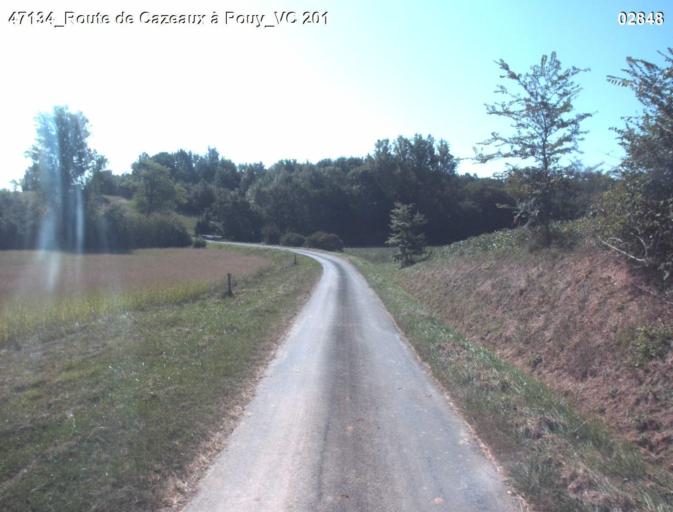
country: FR
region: Aquitaine
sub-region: Departement du Lot-et-Garonne
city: Mezin
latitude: 44.0251
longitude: 0.3103
